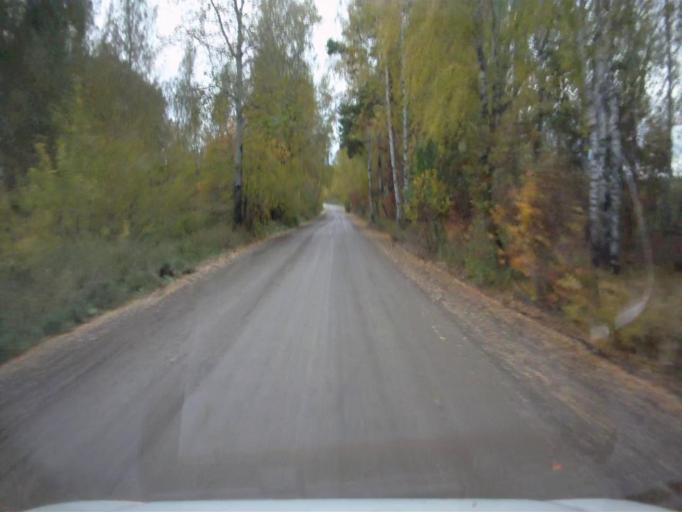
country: RU
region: Sverdlovsk
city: Mikhaylovsk
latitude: 56.1737
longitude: 59.2179
